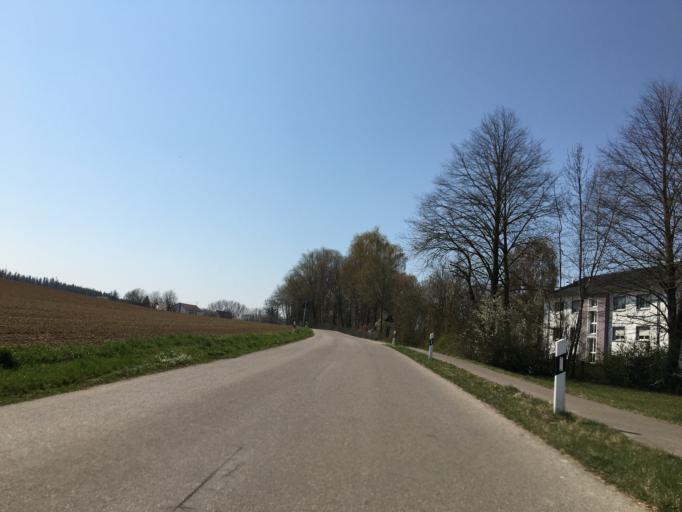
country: DE
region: Bavaria
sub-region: Upper Bavaria
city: Dachau
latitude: 48.2753
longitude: 11.4062
